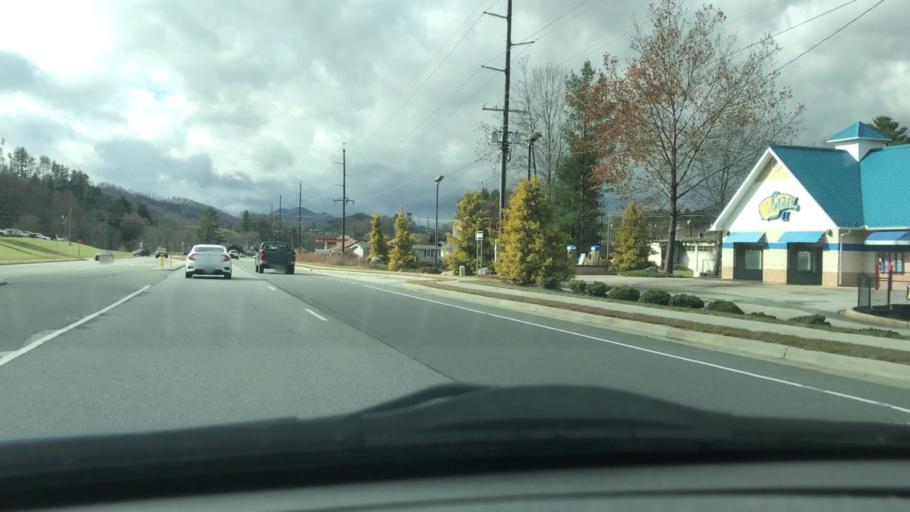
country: US
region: North Carolina
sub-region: Yancey County
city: Burnsville
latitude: 35.9138
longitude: -82.3087
